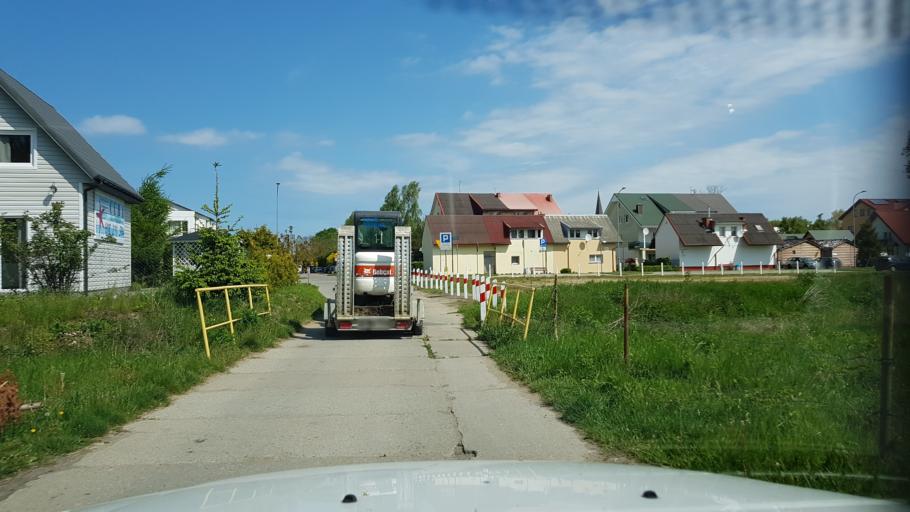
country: PL
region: West Pomeranian Voivodeship
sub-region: Powiat koszalinski
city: Mielno
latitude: 54.2456
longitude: 15.9559
